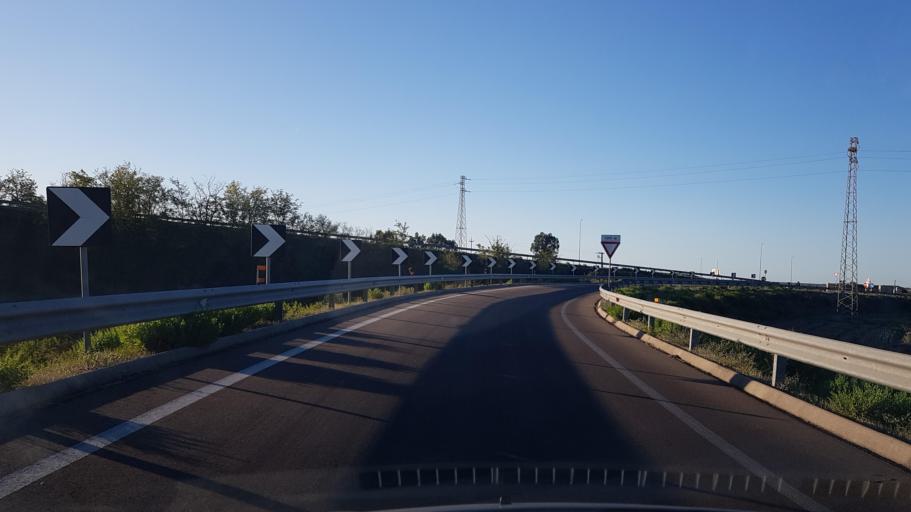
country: IT
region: Apulia
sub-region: Provincia di Brindisi
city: San Pancrazio Salentino
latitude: 40.4140
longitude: 17.8107
